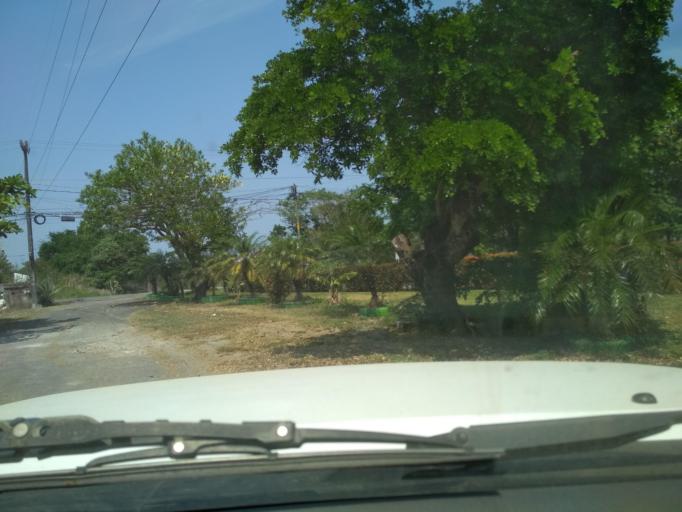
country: MX
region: Veracruz
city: Boca del Rio
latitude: 19.0944
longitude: -96.1199
